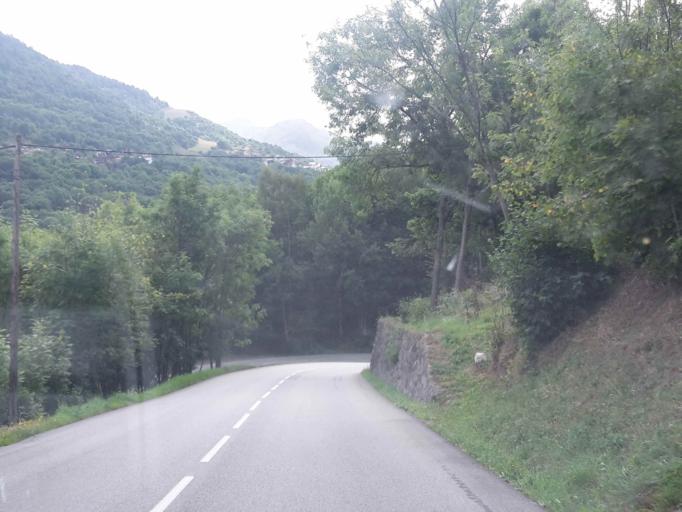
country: FR
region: Rhone-Alpes
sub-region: Departement de la Savoie
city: Saint-Michel-de-Maurienne
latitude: 45.1967
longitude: 6.4679
